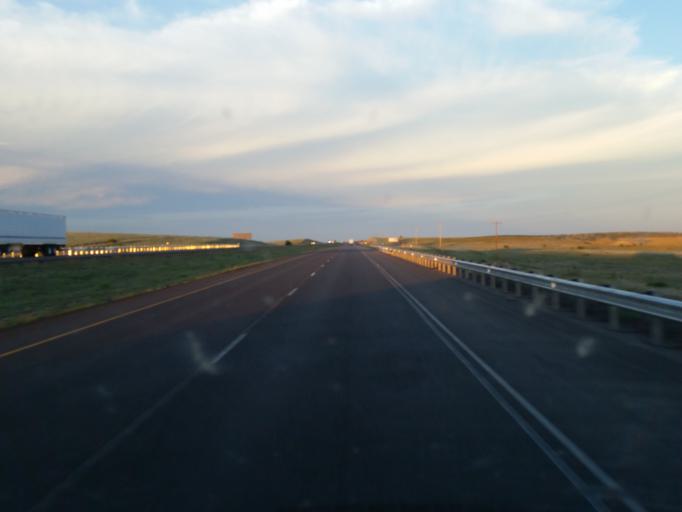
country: US
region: New Mexico
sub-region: Guadalupe County
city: Santa Rosa
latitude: 34.9903
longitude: -105.2720
